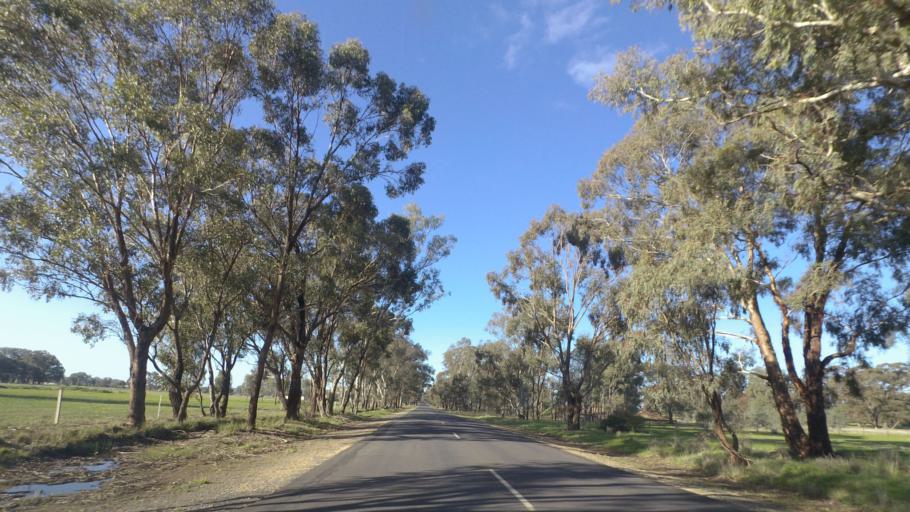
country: AU
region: Victoria
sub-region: Greater Bendigo
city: Epsom
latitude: -36.6601
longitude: 144.4662
